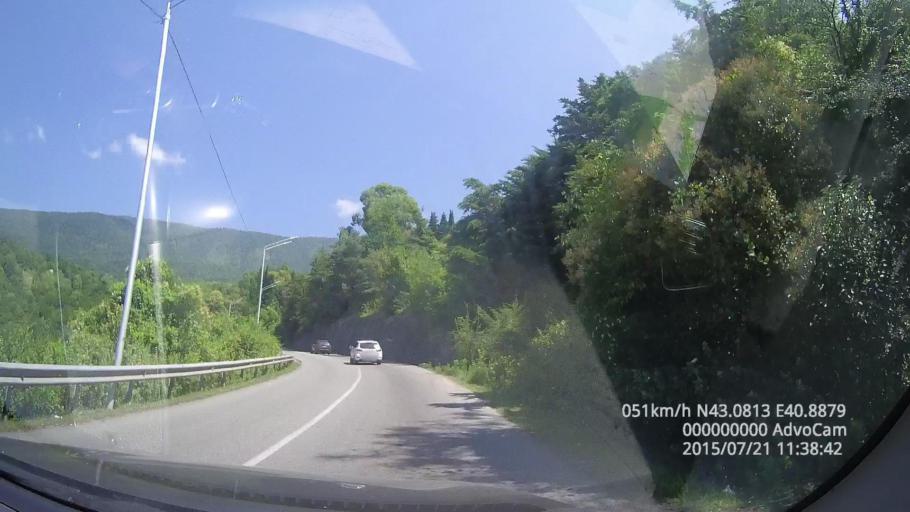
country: GE
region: Abkhazia
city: Stantsiya Novyy Afon
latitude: 43.0816
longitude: 40.8878
